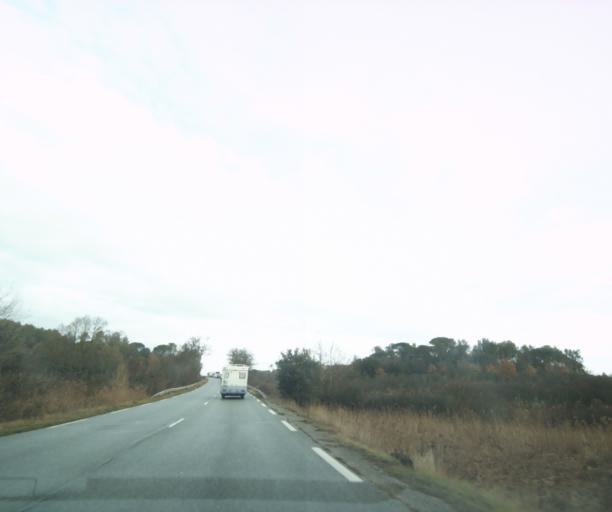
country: FR
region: Provence-Alpes-Cote d'Azur
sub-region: Departement du Var
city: Tourves
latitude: 43.4161
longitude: 5.9088
